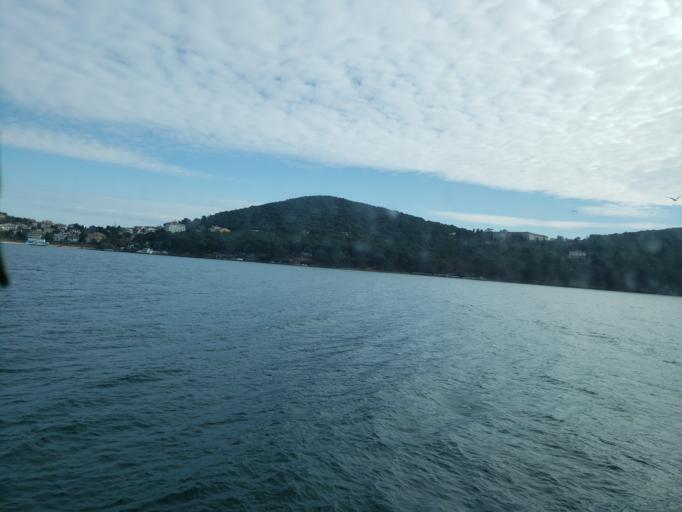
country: TR
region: Istanbul
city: Adalan
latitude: 40.8825
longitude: 29.0824
